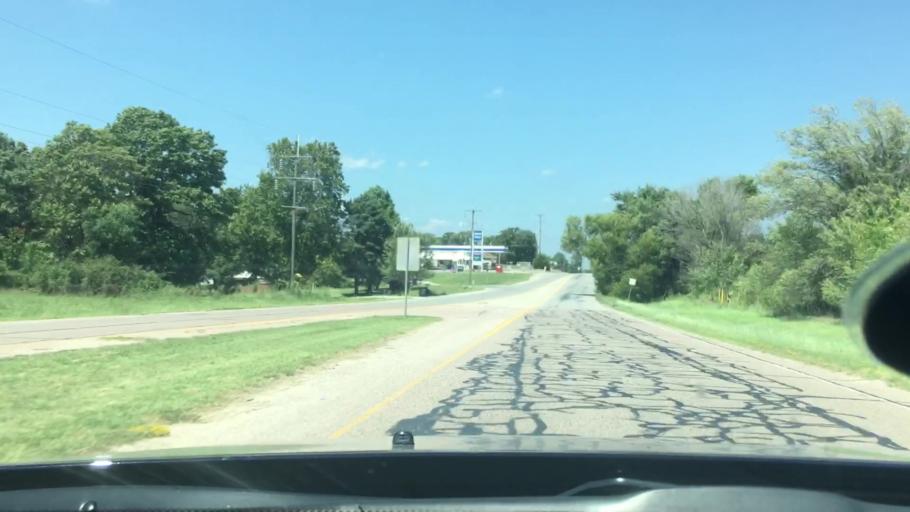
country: US
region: Oklahoma
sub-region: Pontotoc County
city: Ada
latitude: 34.8156
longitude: -96.6785
